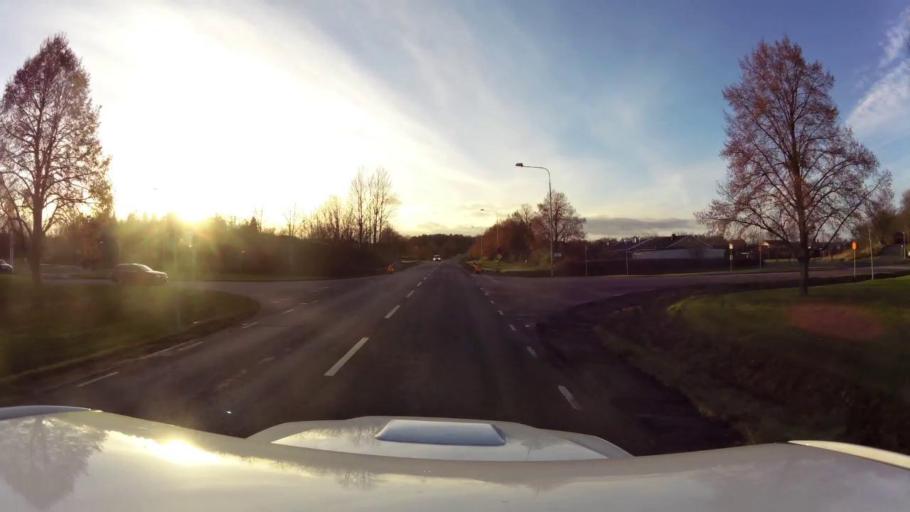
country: SE
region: OEstergoetland
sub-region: Linkopings Kommun
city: Linkoping
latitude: 58.3835
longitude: 15.6516
